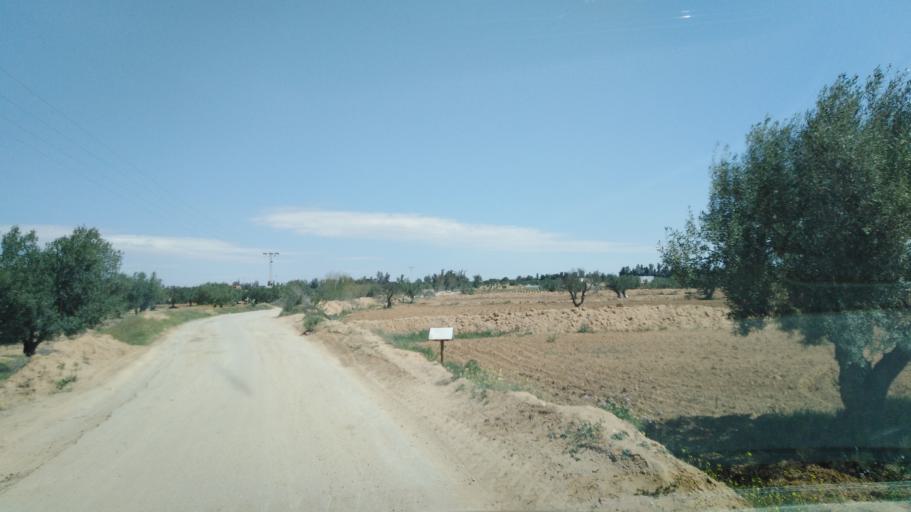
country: TN
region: Safaqis
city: Sfax
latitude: 34.7527
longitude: 10.5281
